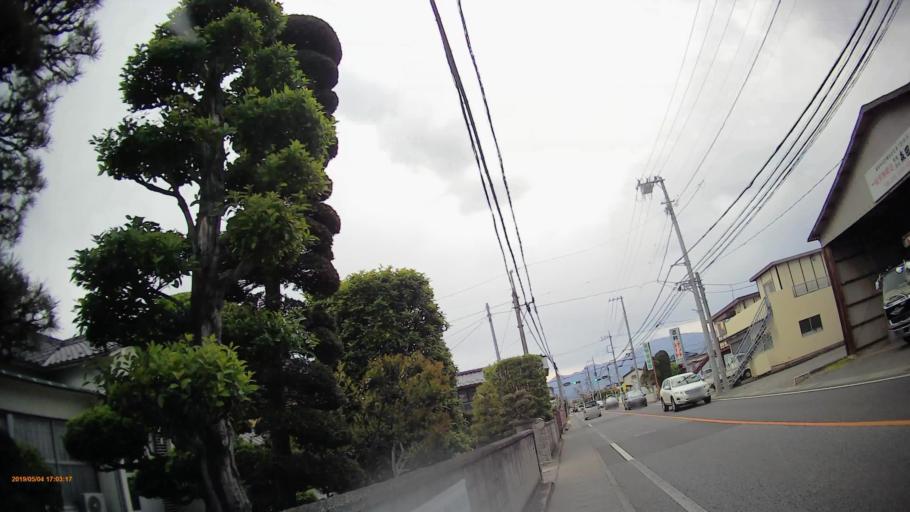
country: JP
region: Yamanashi
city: Isawa
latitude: 35.6532
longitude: 138.6202
